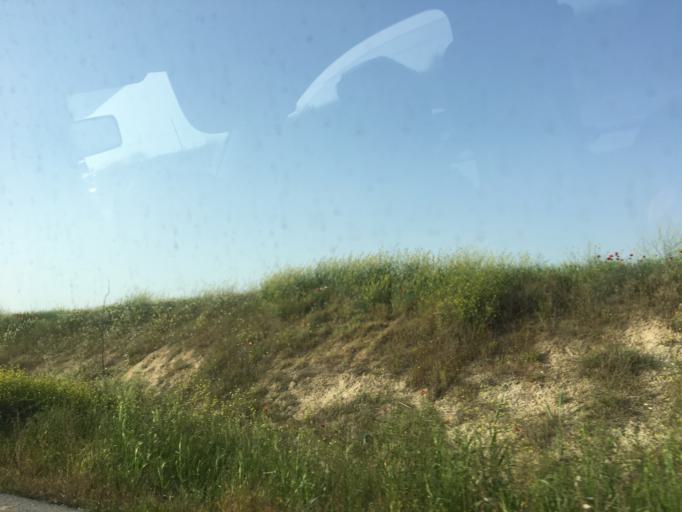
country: TR
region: Manisa
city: Ahmetli
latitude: 38.5658
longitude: 28.0363
